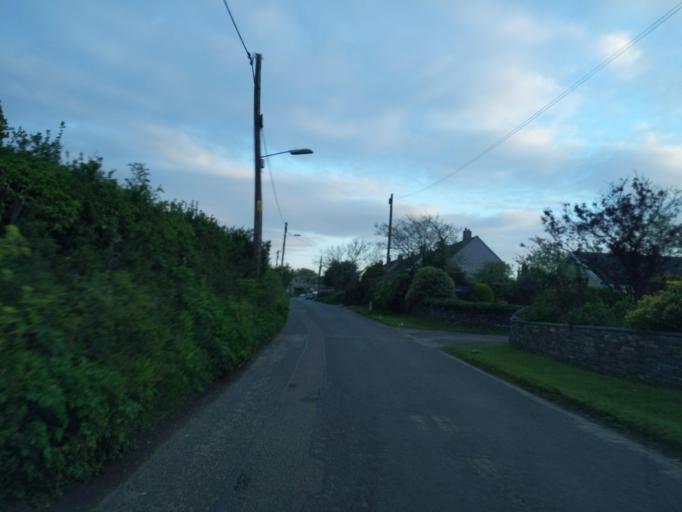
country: GB
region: England
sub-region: Cornwall
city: Polzeath
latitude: 50.5605
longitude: -4.8726
